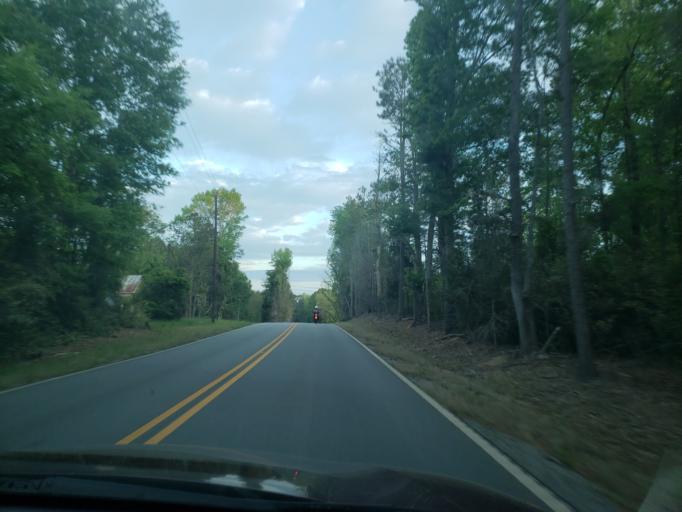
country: US
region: Alabama
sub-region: Tallapoosa County
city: Dadeville
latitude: 32.7057
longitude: -85.7615
